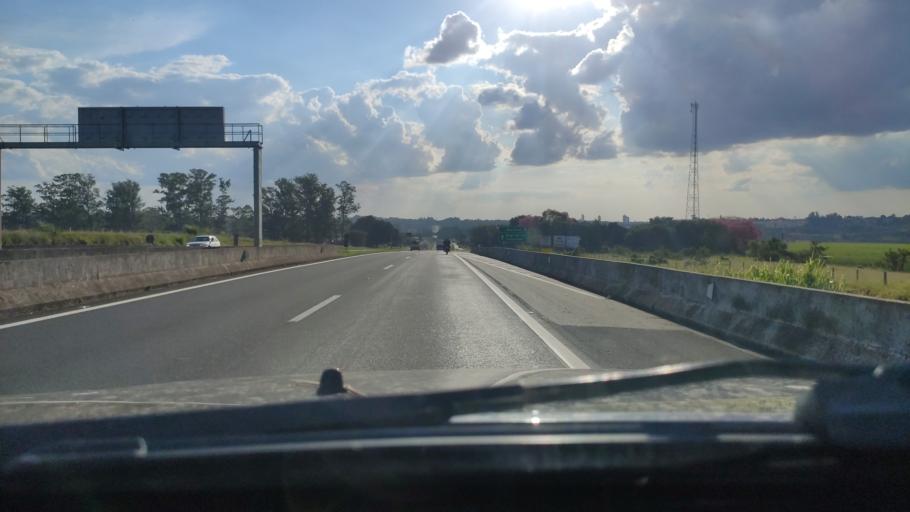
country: BR
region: Sao Paulo
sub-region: Mogi-Mirim
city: Mogi Mirim
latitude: -22.4556
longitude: -46.9172
